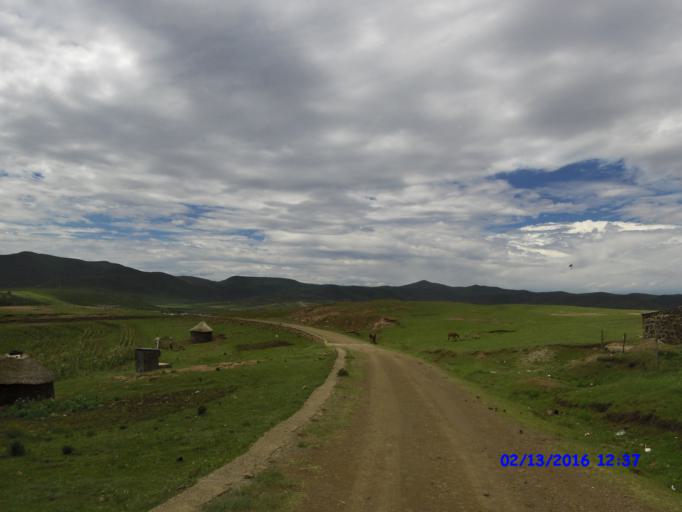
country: LS
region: Maseru
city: Nako
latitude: -29.8375
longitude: 28.0263
